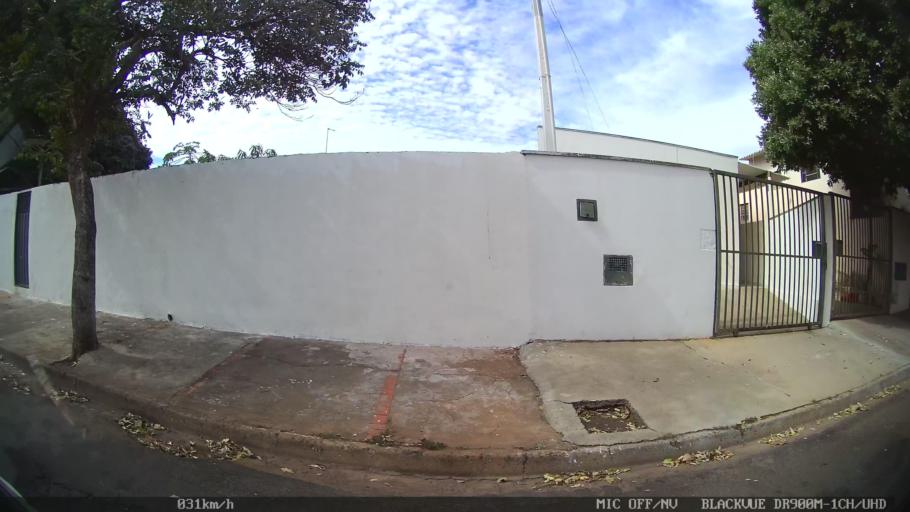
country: BR
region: Sao Paulo
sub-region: Catanduva
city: Catanduva
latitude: -21.1508
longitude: -48.9693
